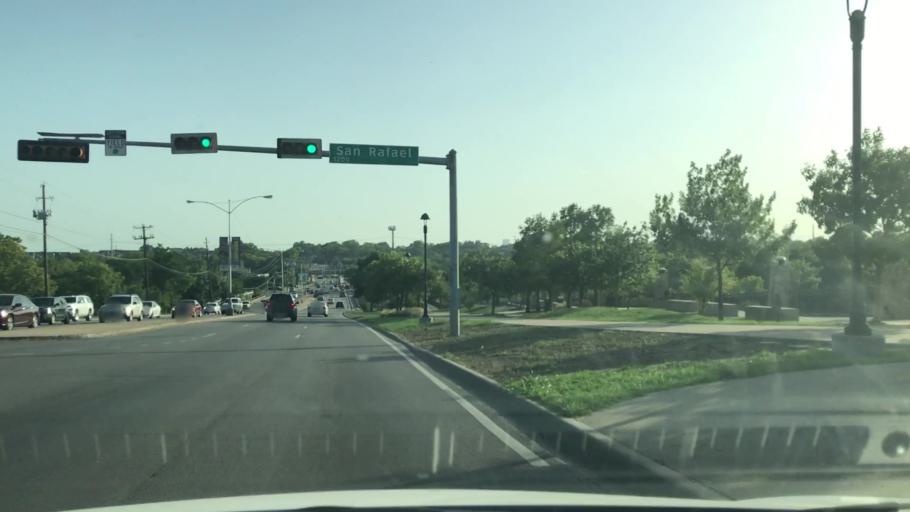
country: US
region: Texas
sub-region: Dallas County
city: Highland Park
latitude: 32.8146
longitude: -96.7244
